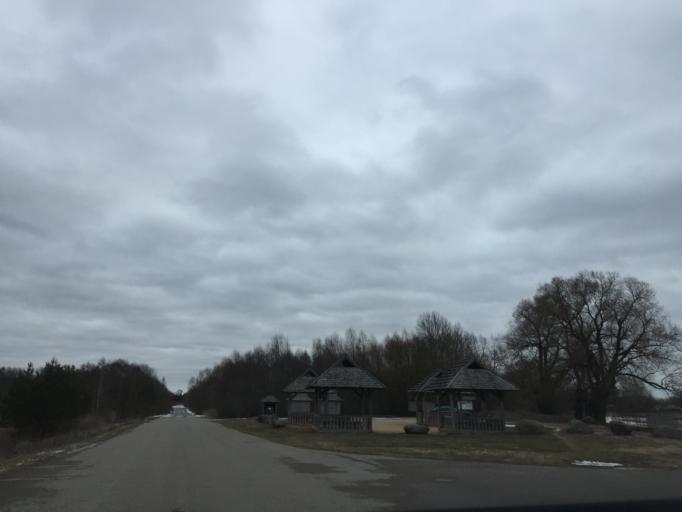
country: LT
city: Zagare
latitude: 56.3541
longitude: 23.2236
